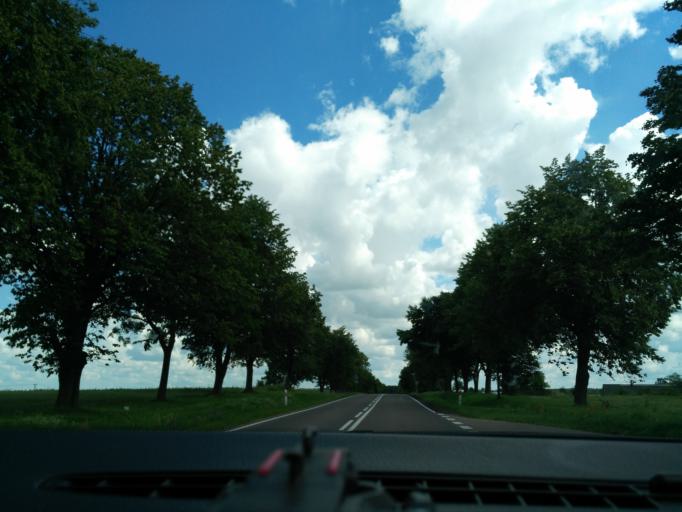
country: PL
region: Podlasie
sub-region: Powiat siemiatycki
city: Dziadkowice
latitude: 52.6000
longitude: 22.9689
